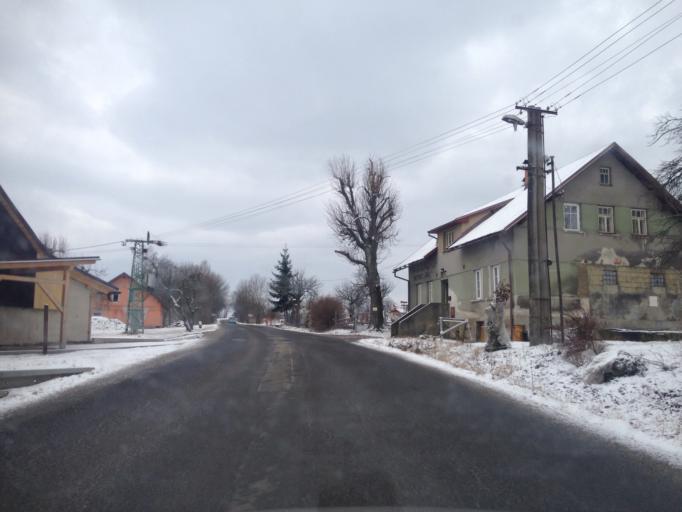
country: CZ
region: Liberecky
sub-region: Okres Semily
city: Vysoke nad Jizerou
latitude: 50.6645
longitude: 15.4149
